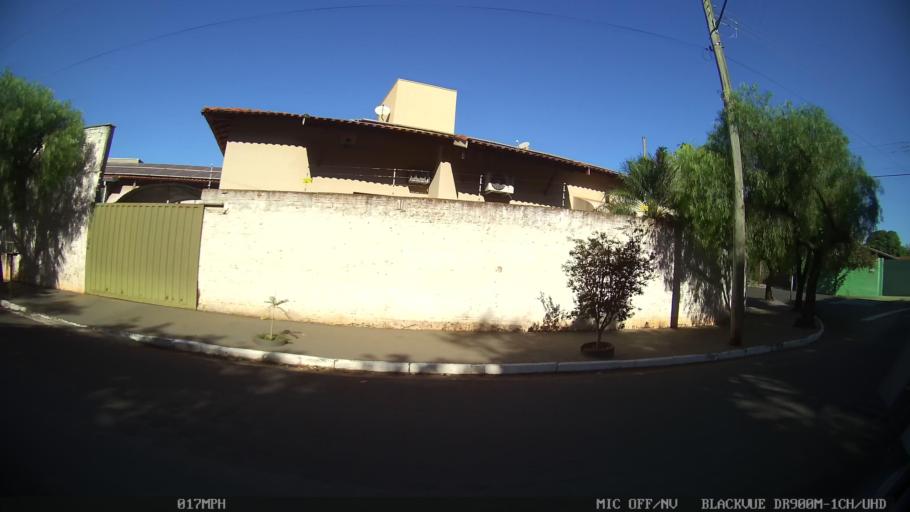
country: BR
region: Sao Paulo
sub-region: Olimpia
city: Olimpia
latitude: -20.7307
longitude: -48.9196
